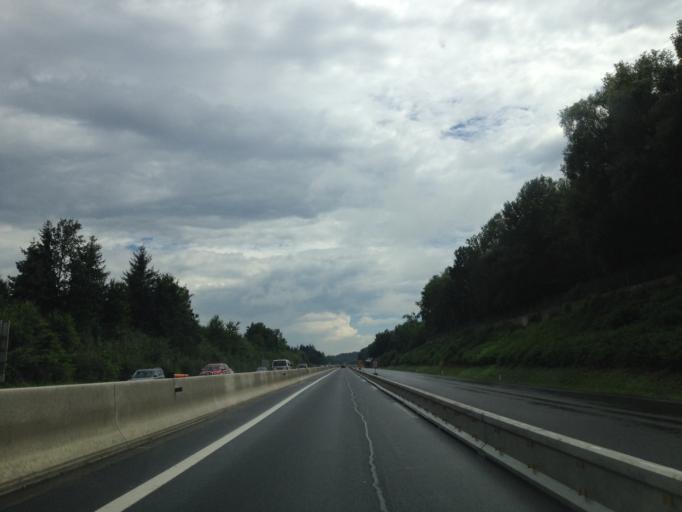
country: AT
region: Styria
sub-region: Politischer Bezirk Hartberg-Fuerstenfeld
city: Bad Waltersdorf
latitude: 47.1718
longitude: 15.9979
